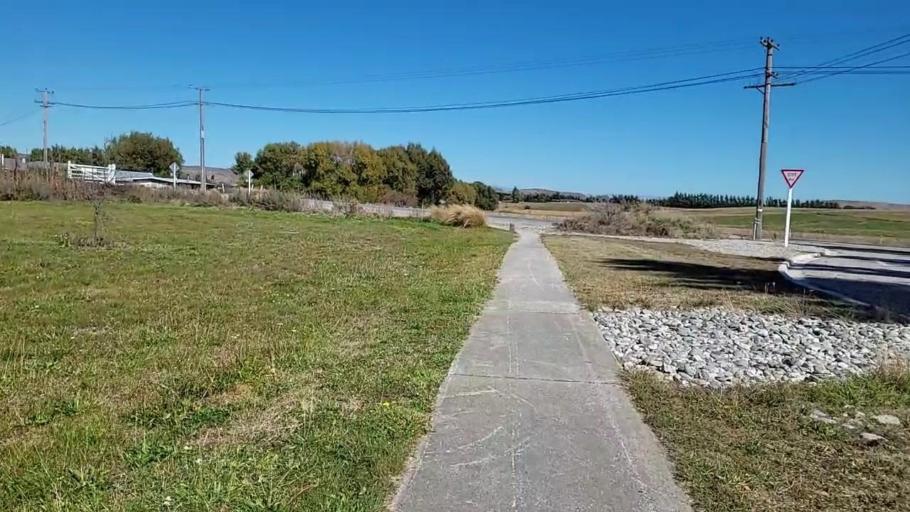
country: NZ
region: Otago
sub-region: Queenstown-Lakes District
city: Wanaka
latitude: -45.0918
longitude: 169.6024
